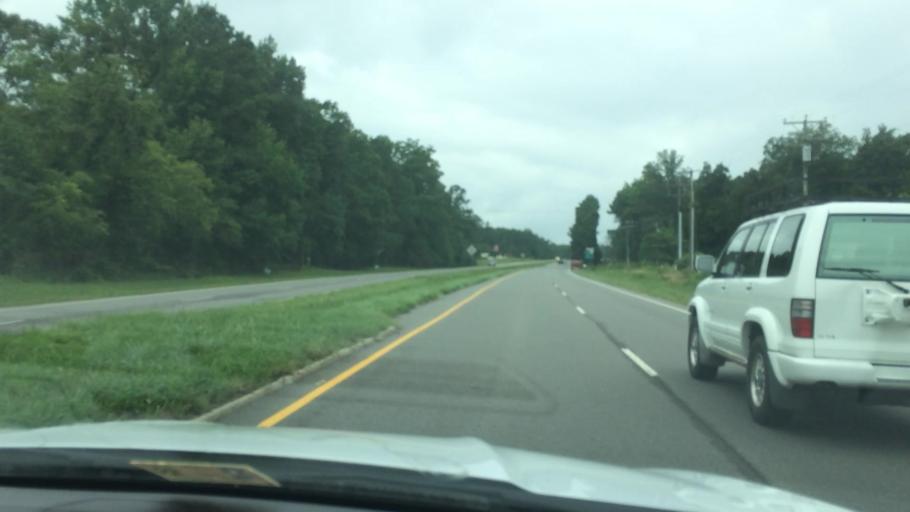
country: US
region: Virginia
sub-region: King William County
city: West Point
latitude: 37.5189
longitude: -76.8327
